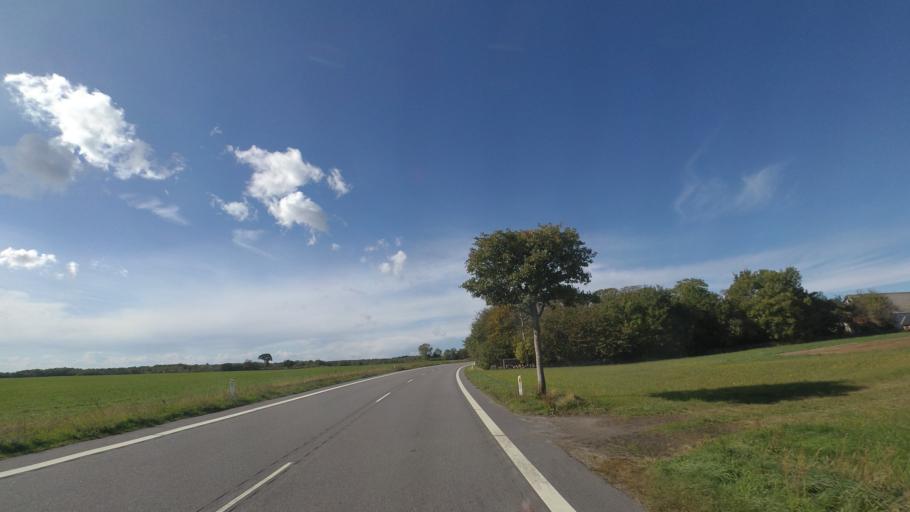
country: DK
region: Capital Region
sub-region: Bornholm Kommune
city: Ronne
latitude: 55.0748
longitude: 14.7804
